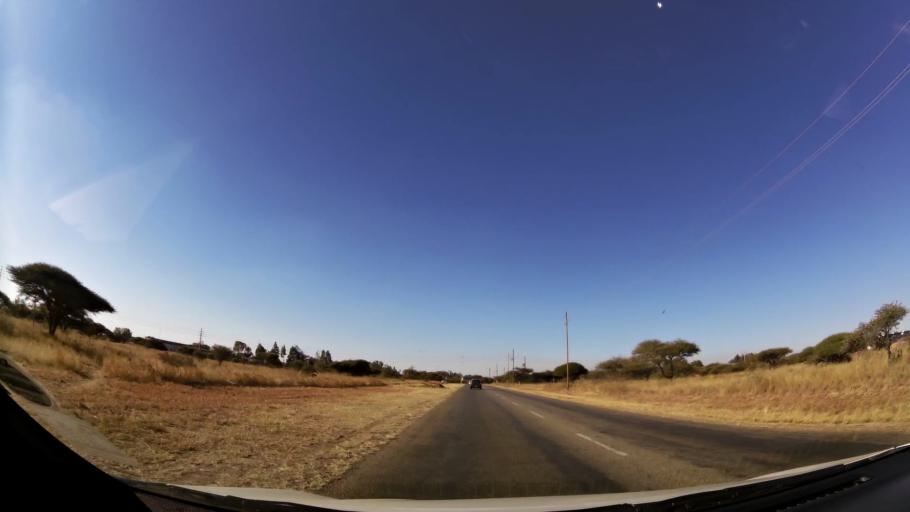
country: ZA
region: Limpopo
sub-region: Capricorn District Municipality
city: Polokwane
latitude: -23.8724
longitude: 29.4827
